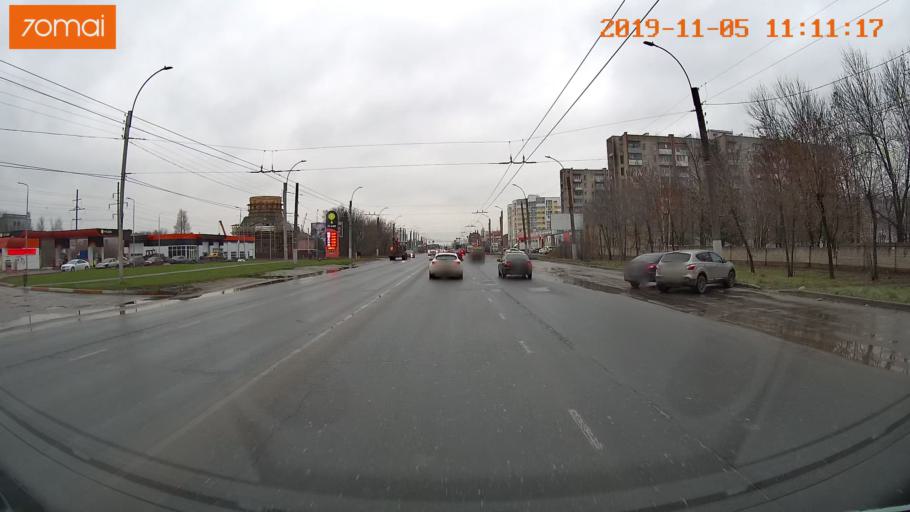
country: RU
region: Ivanovo
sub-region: Gorod Ivanovo
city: Ivanovo
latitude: 56.9650
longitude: 40.9664
